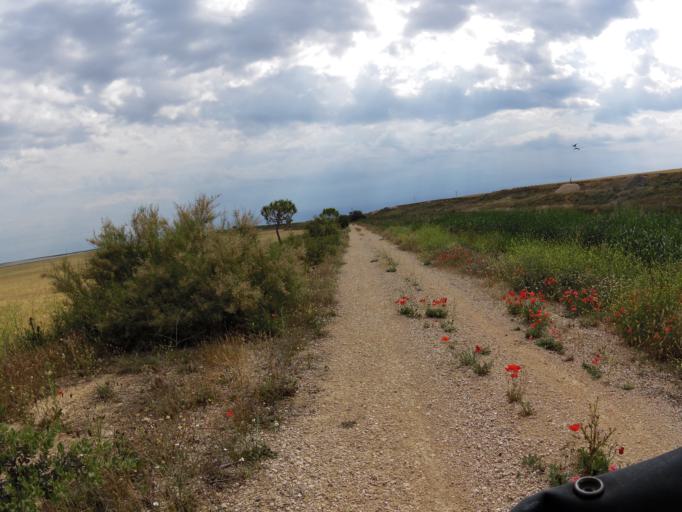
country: ES
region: Castille-La Mancha
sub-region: Provincia de Albacete
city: Albacete
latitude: 39.0396
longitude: -1.7827
